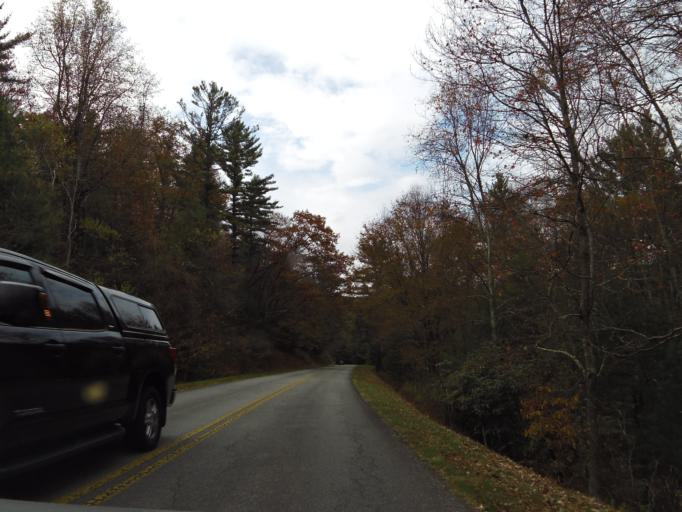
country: US
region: North Carolina
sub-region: Alleghany County
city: Sparta
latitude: 36.3899
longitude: -81.2071
